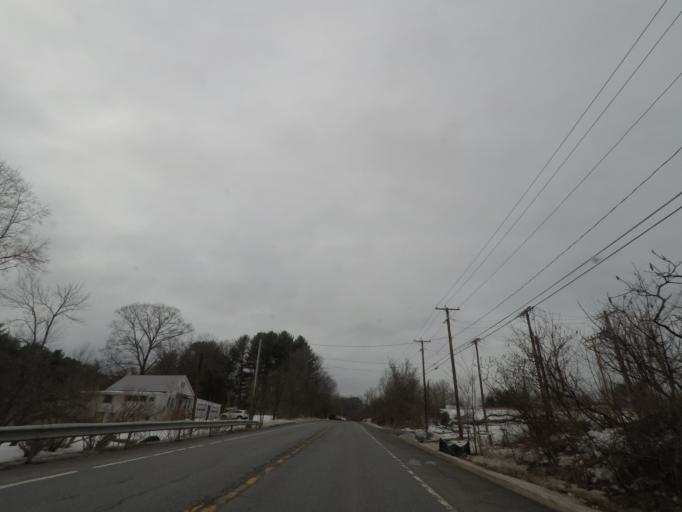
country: US
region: New York
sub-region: Schenectady County
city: Rotterdam
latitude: 42.7289
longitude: -73.9697
